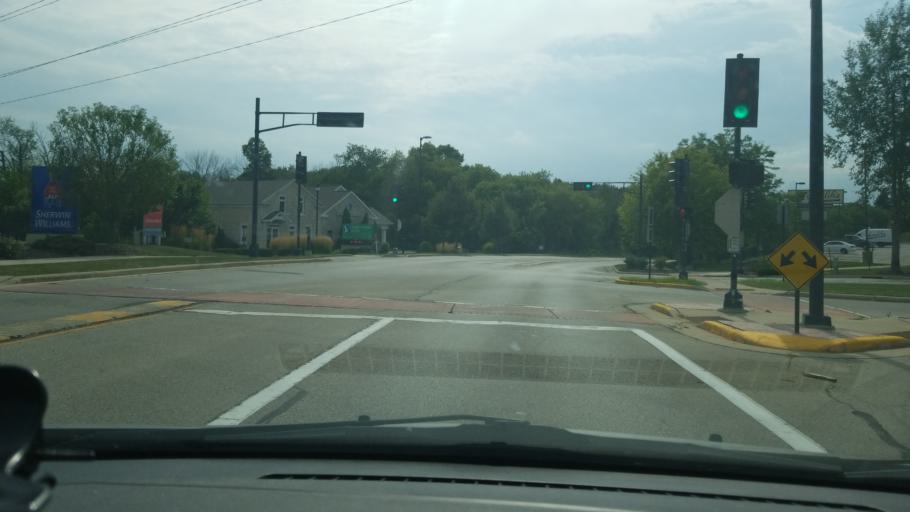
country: US
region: Wisconsin
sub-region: Ozaukee County
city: Grafton
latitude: 43.3023
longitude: -87.9643
